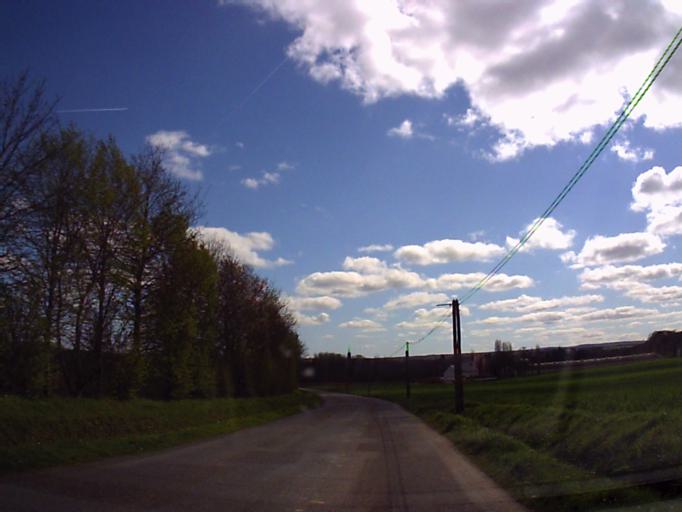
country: FR
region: Brittany
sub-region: Departement d'Ille-et-Vilaine
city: Gael
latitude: 48.1354
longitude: -2.1581
